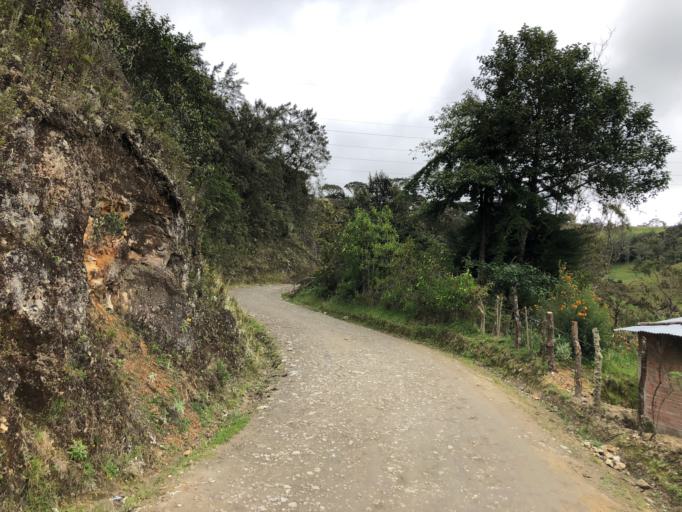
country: CO
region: Cauca
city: Totoro
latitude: 2.4979
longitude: -76.3554
